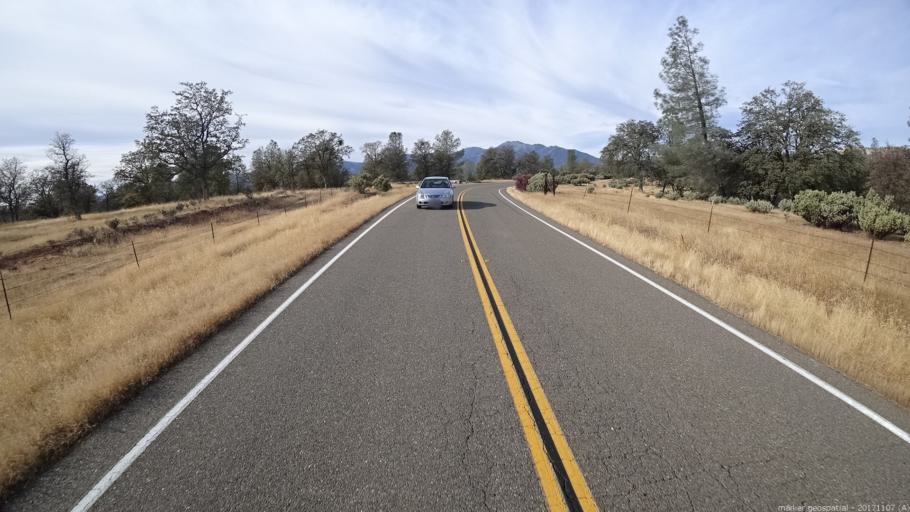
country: US
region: California
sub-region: Shasta County
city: Shasta
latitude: 40.4951
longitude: -122.5191
